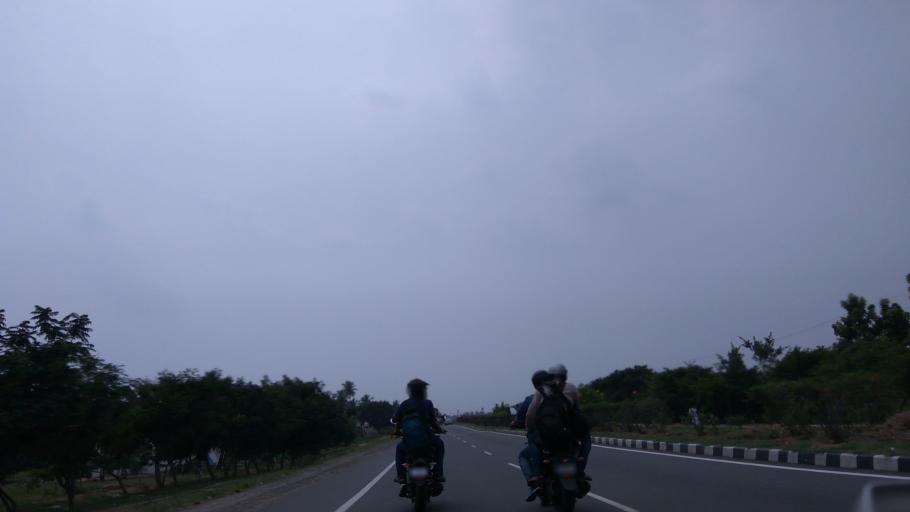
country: IN
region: Tamil Nadu
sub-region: Krishnagiri
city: Kaverippattanam
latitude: 12.3274
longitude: 78.2109
